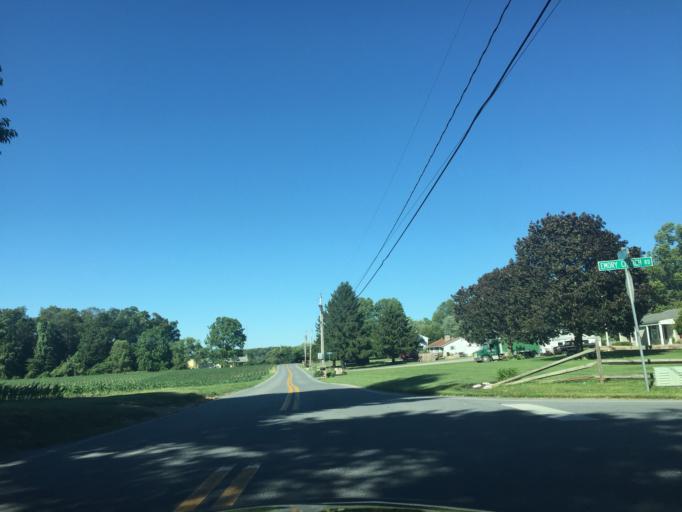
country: US
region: Maryland
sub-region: Carroll County
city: Hampstead
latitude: 39.5500
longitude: -76.8614
